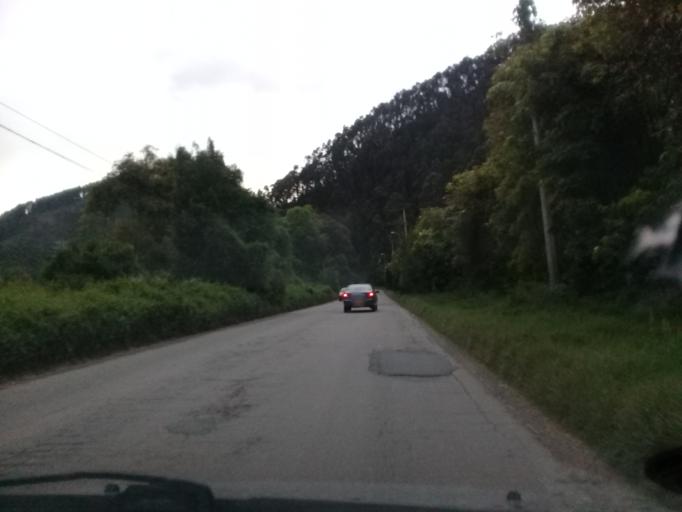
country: CO
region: Cundinamarca
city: Tabio
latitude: 4.9264
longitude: -74.0610
